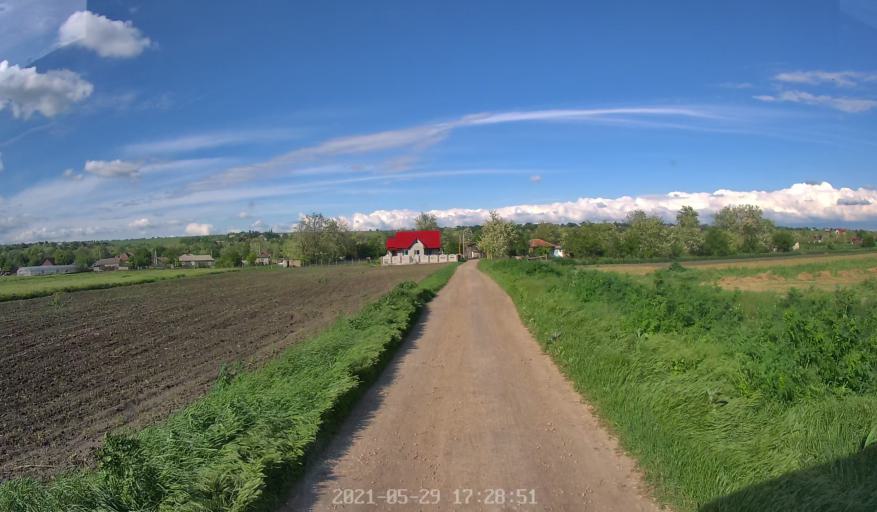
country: MD
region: Laloveni
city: Ialoveni
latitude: 46.8341
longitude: 28.8417
